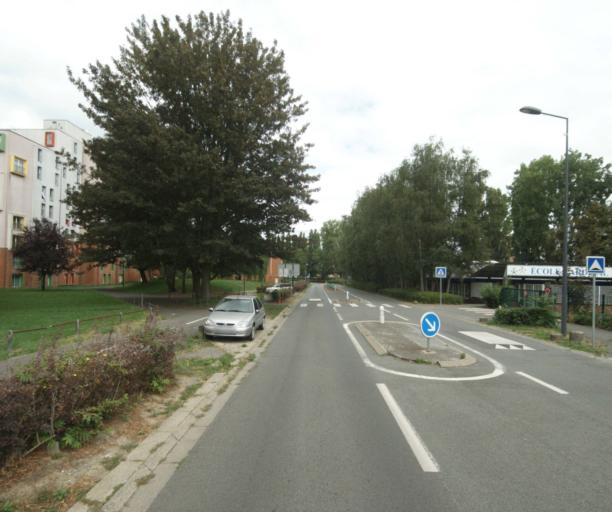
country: FR
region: Nord-Pas-de-Calais
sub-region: Departement du Nord
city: Mons-en-Baroeul
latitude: 50.6208
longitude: 3.1384
